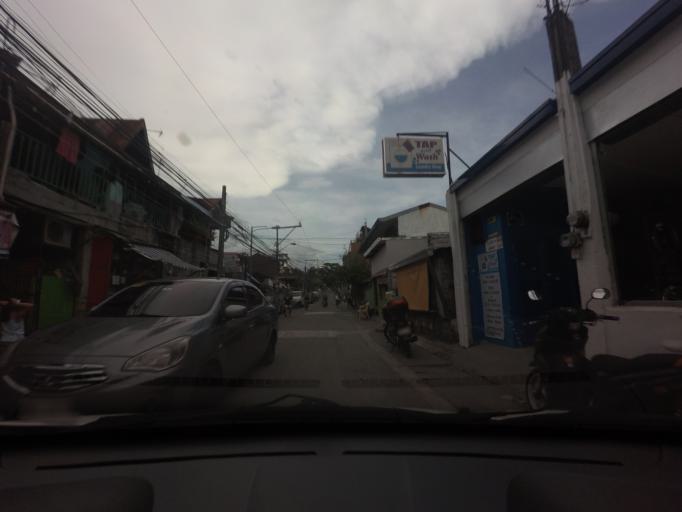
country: PH
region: Calabarzon
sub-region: Province of Rizal
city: Pateros
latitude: 14.5488
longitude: 121.0598
